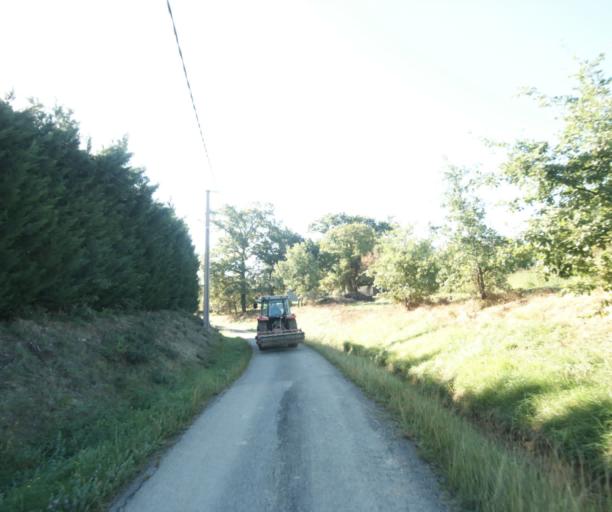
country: FR
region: Midi-Pyrenees
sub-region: Departement du Gers
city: Gondrin
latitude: 43.8362
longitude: 0.2809
